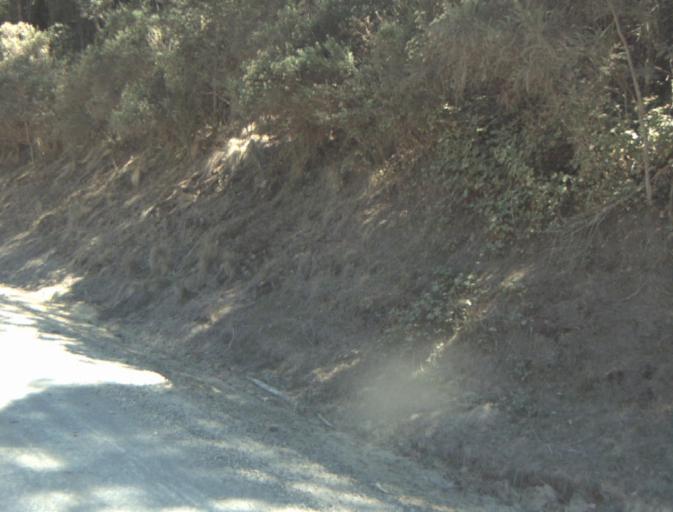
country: AU
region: Tasmania
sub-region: Dorset
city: Scottsdale
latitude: -41.3216
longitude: 147.4146
